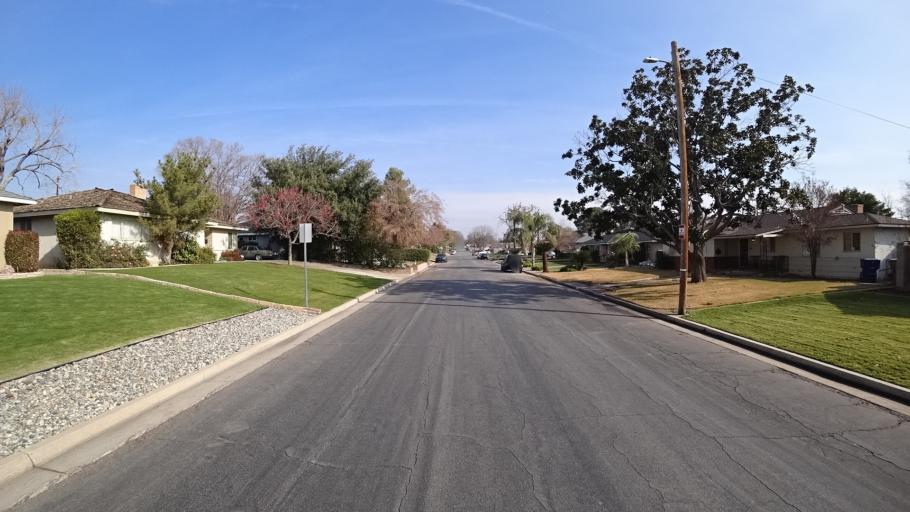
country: US
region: California
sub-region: Kern County
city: Oildale
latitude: 35.4039
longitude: -118.9746
